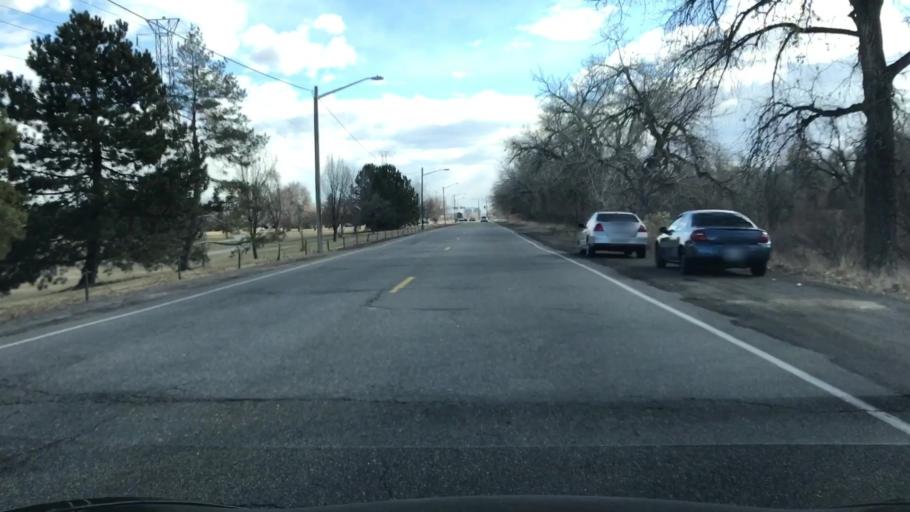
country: US
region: Colorado
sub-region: Arapahoe County
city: Glendale
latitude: 39.6935
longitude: -104.9167
